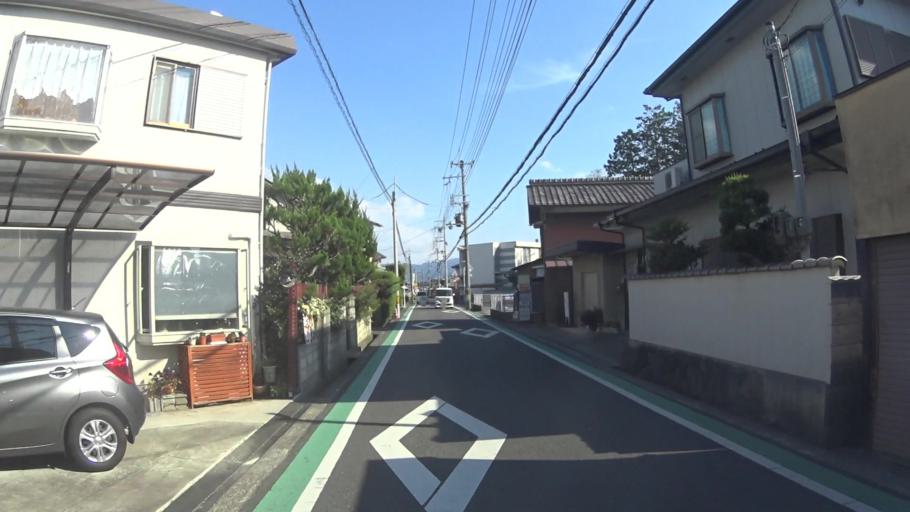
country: JP
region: Kyoto
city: Kameoka
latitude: 35.0310
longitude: 135.5560
